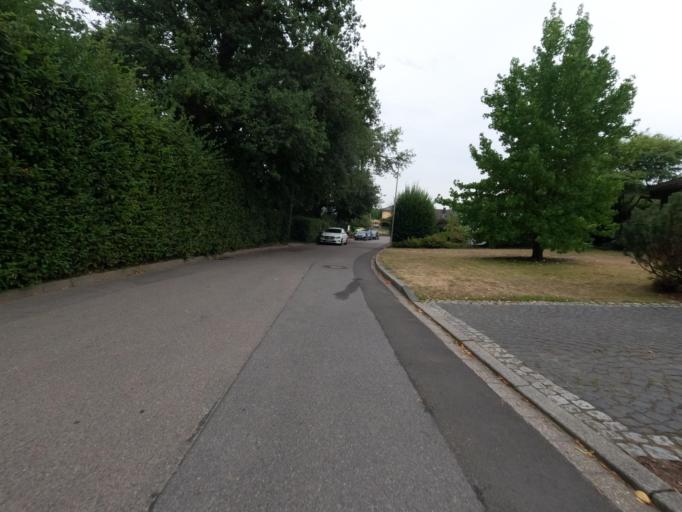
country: DE
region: North Rhine-Westphalia
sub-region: Regierungsbezirk Koln
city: Linnich
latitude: 50.9466
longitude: 6.2973
